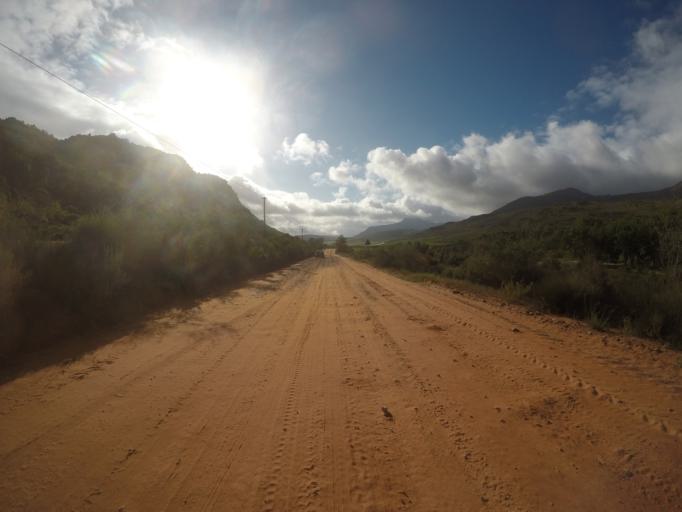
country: ZA
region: Western Cape
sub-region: West Coast District Municipality
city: Clanwilliam
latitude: -32.3430
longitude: 18.8115
